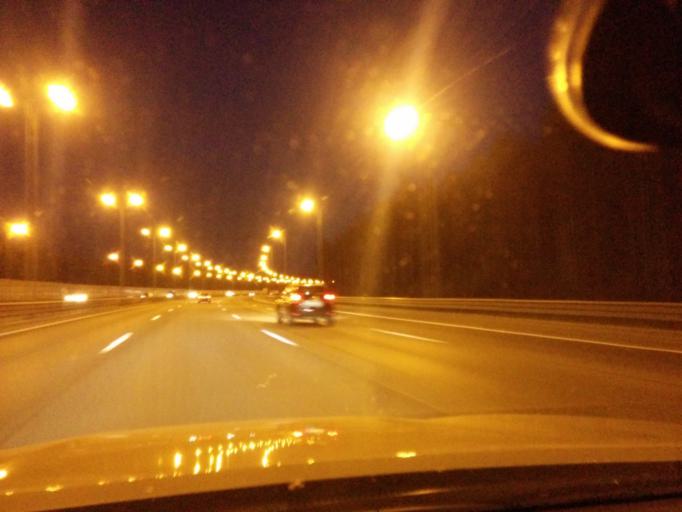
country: RU
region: St.-Petersburg
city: Krasnogvargeisky
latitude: 59.9733
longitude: 30.5438
